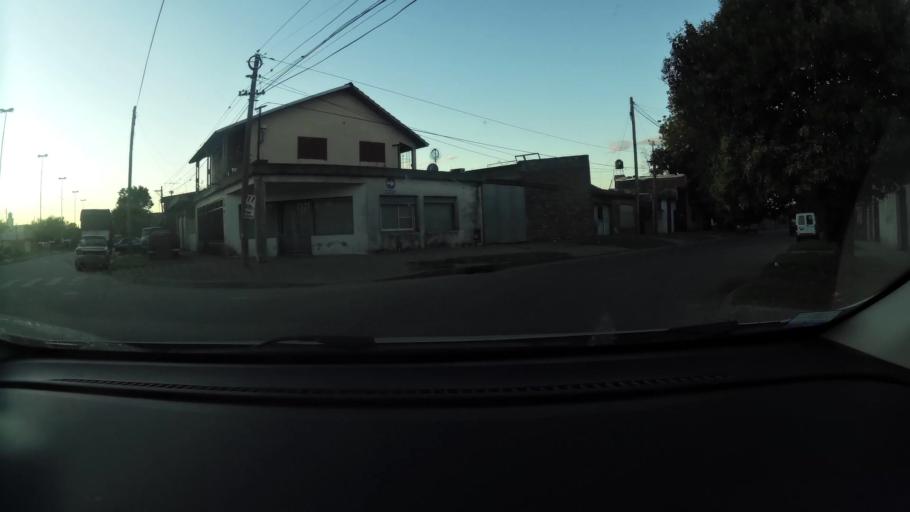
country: AR
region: Santa Fe
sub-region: Departamento de Rosario
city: Rosario
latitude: -32.9714
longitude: -60.6887
